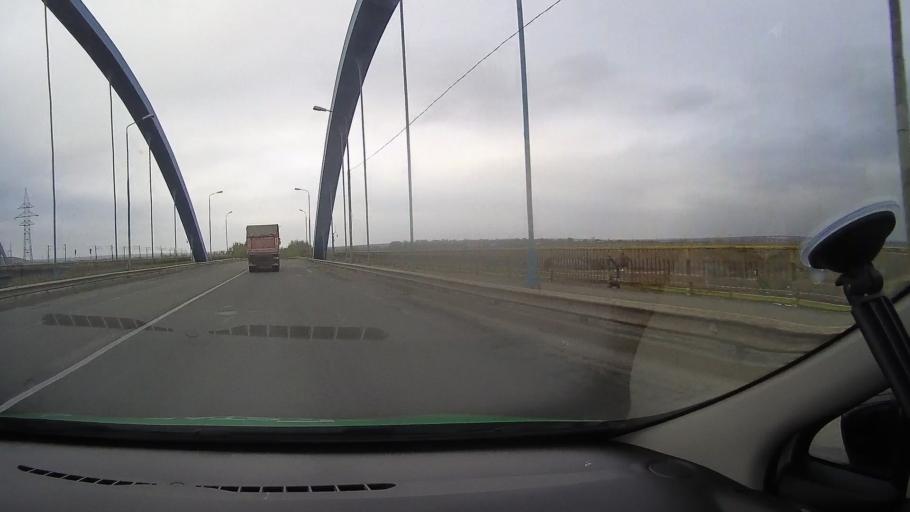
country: RO
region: Constanta
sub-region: Comuna Poarta Alba
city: Poarta Alba
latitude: 44.2174
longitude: 28.3892
